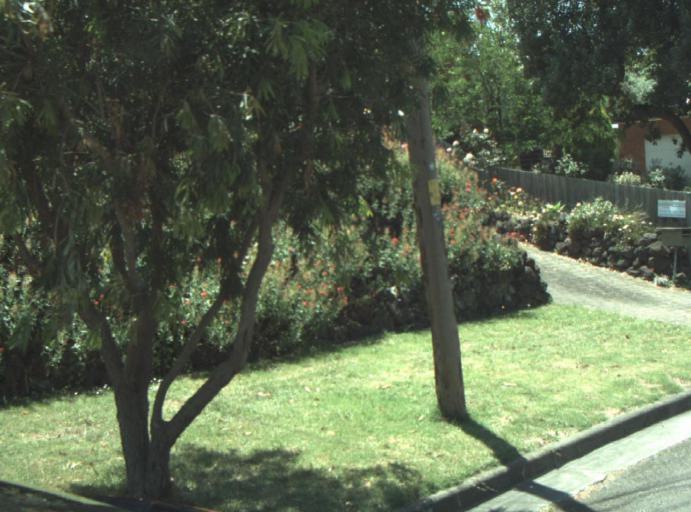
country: AU
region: Victoria
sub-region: Greater Geelong
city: Wandana Heights
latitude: -38.1608
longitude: 144.3193
